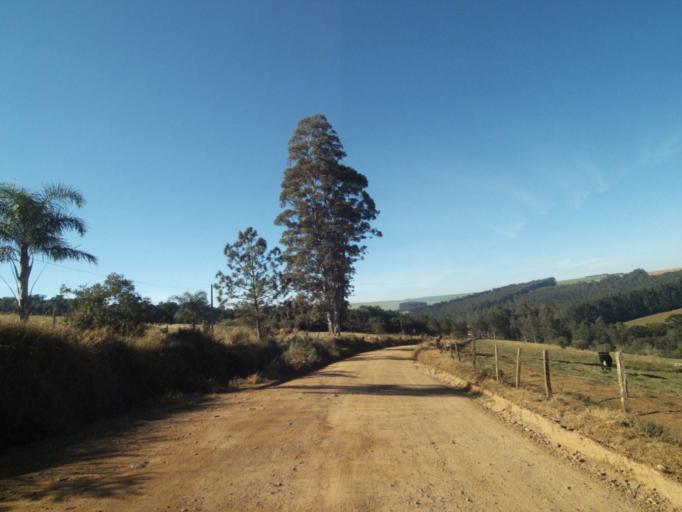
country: BR
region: Parana
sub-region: Tibagi
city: Tibagi
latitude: -24.5282
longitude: -50.3797
